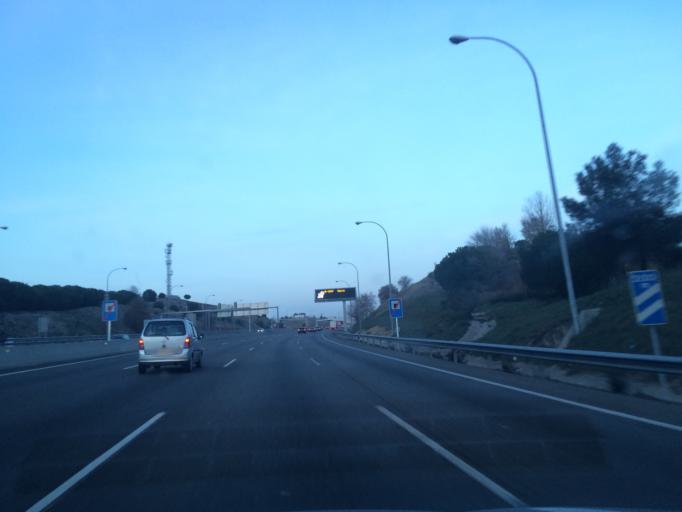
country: ES
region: Madrid
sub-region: Provincia de Madrid
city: Fuencarral-El Pardo
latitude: 40.4874
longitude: -3.7413
